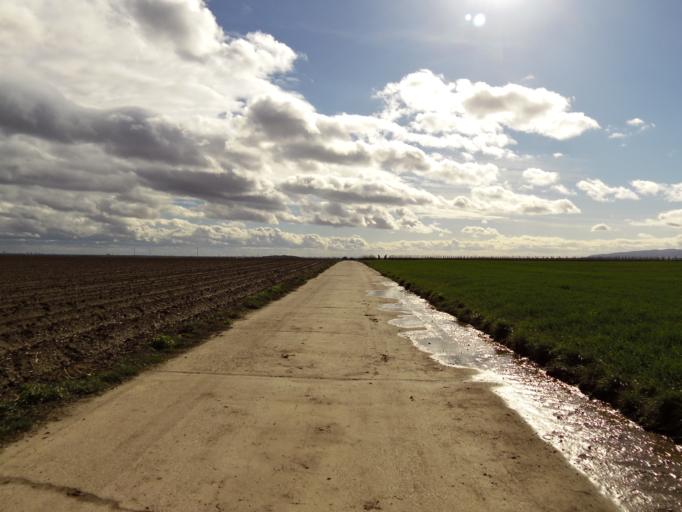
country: DE
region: Rheinland-Pfalz
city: Dirmstein
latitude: 49.5822
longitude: 8.2614
